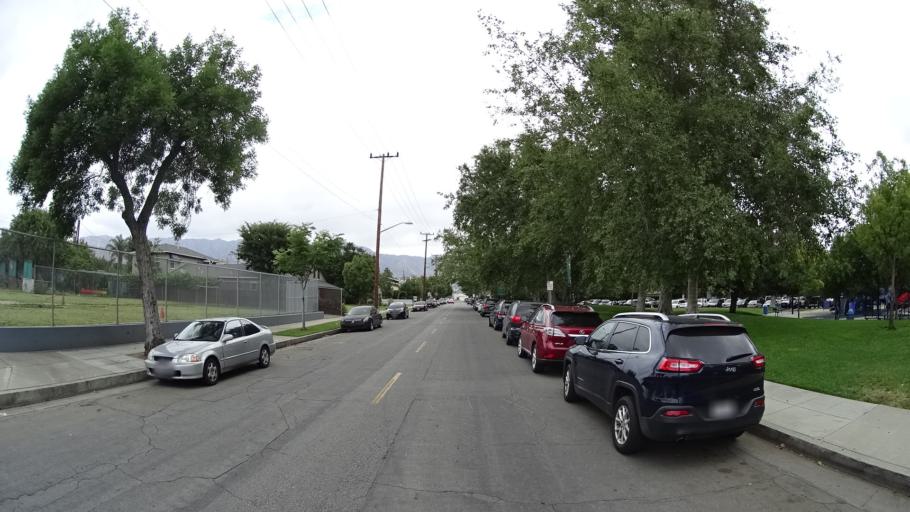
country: US
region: California
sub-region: Los Angeles County
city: Burbank
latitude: 34.1730
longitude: -118.3197
